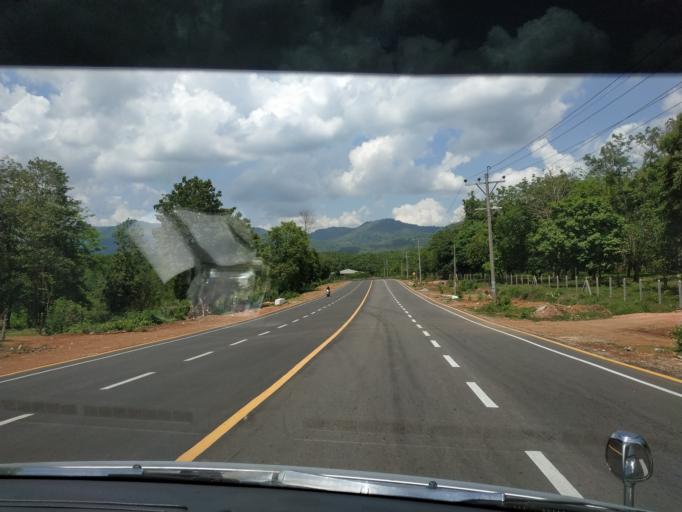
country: MM
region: Mon
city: Kyaikto
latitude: 17.3897
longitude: 97.0696
